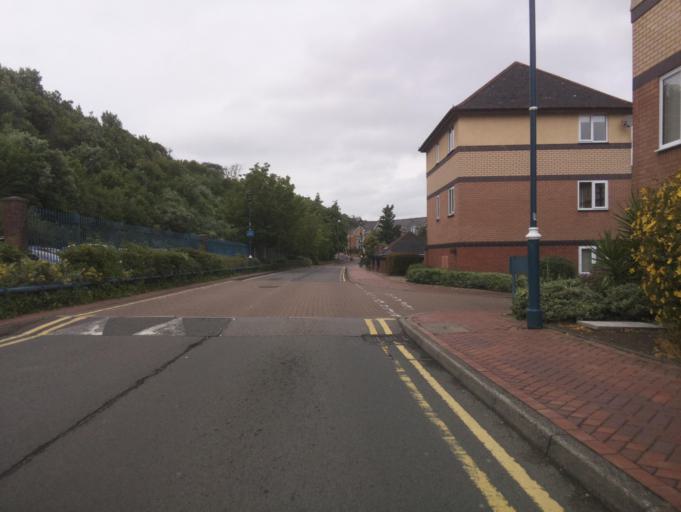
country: GB
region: Wales
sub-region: Vale of Glamorgan
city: Penarth
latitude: 51.4442
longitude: -3.1759
